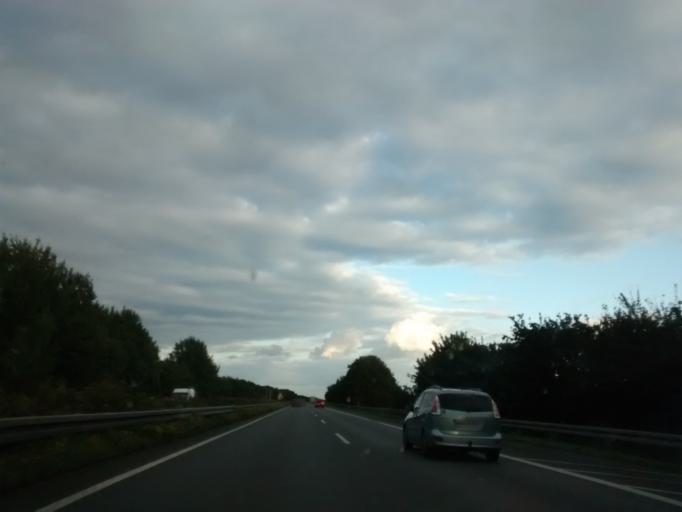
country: DE
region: North Rhine-Westphalia
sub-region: Regierungsbezirk Munster
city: Horstel
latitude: 52.2902
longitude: 7.5513
